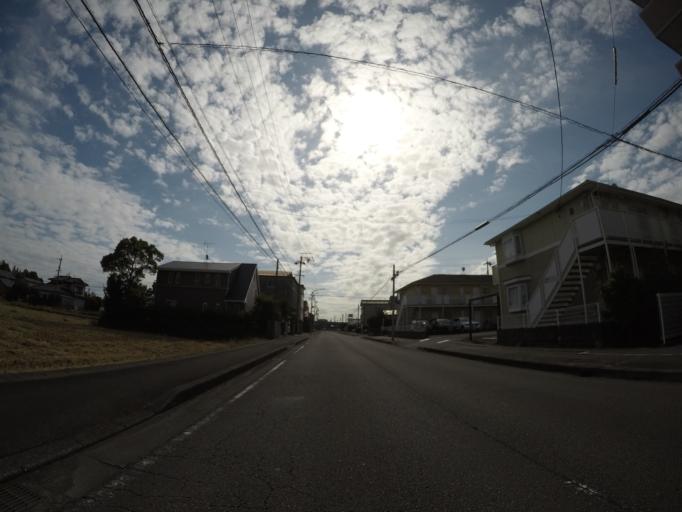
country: JP
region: Shizuoka
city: Yaizu
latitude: 34.8847
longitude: 138.3211
